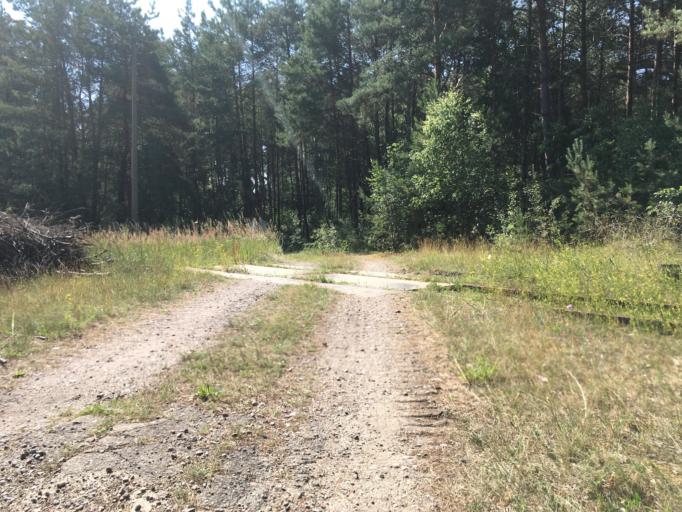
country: DE
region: Brandenburg
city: Milmersdorf
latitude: 53.0955
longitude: 13.6449
